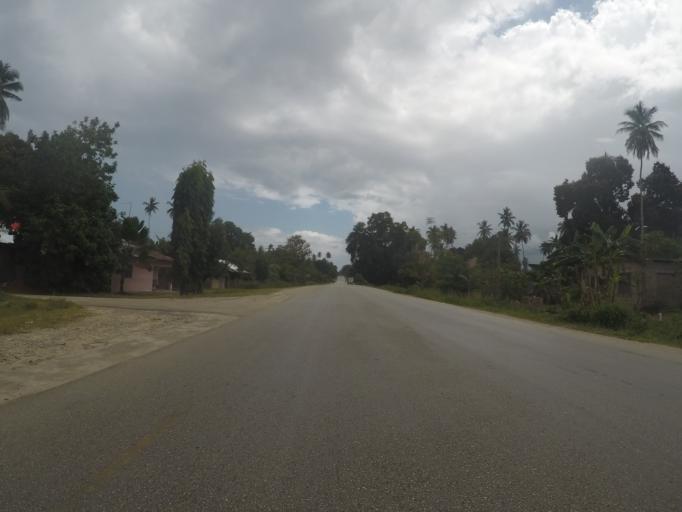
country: TZ
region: Zanzibar North
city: Mkokotoni
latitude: -6.0103
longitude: 39.2020
